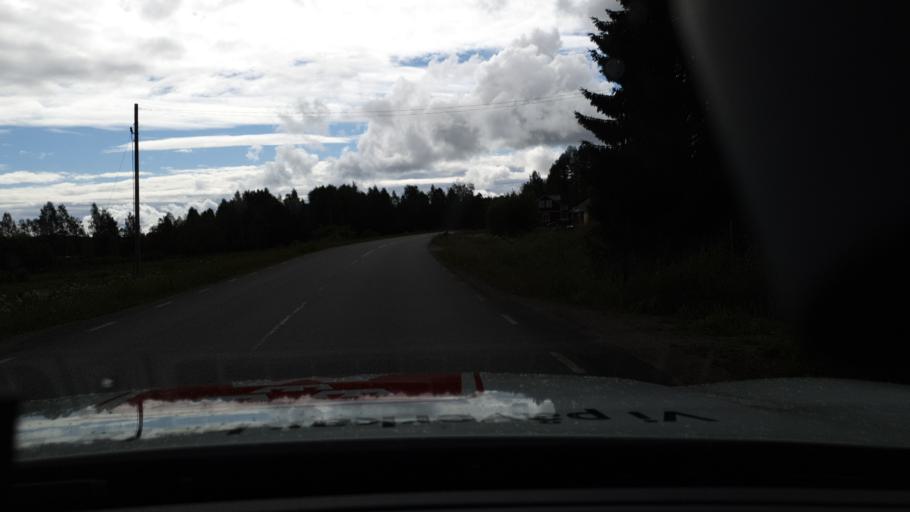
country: SE
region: Norrbotten
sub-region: Lulea Kommun
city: Sodra Sunderbyn
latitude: 65.5106
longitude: 21.8605
